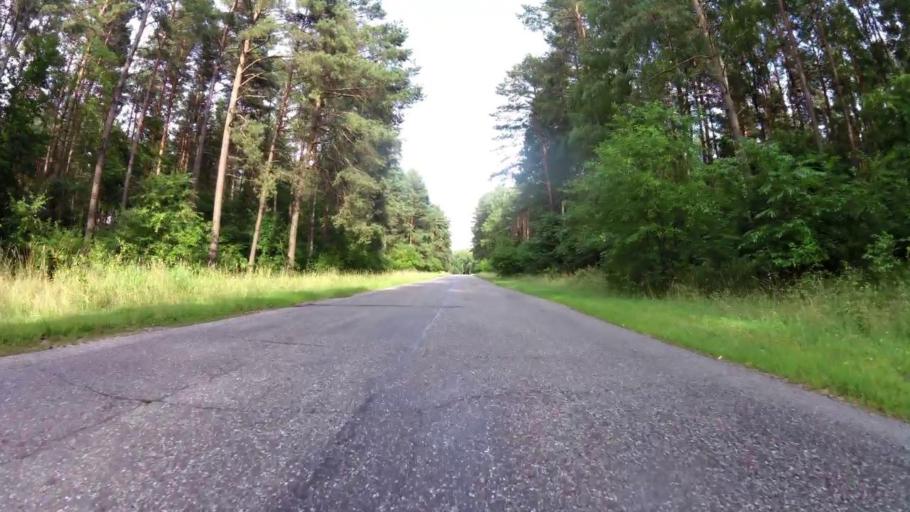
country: PL
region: West Pomeranian Voivodeship
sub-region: Powiat drawski
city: Drawsko Pomorskie
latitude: 53.4681
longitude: 15.7459
